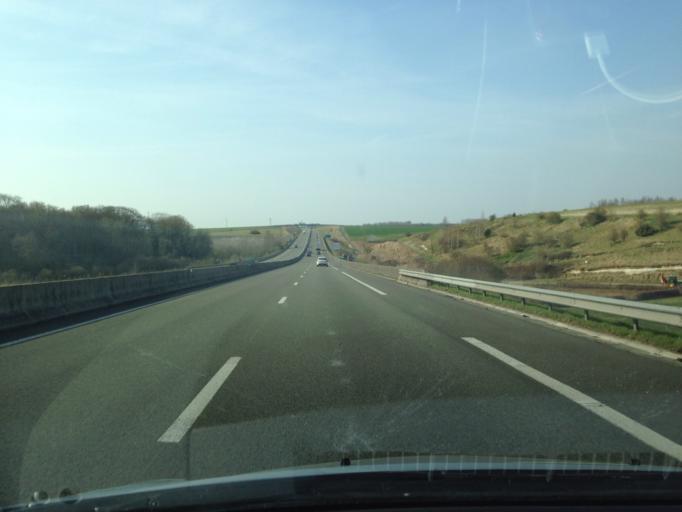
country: FR
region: Picardie
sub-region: Departement de la Somme
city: Abbeville
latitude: 50.1424
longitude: 1.8055
